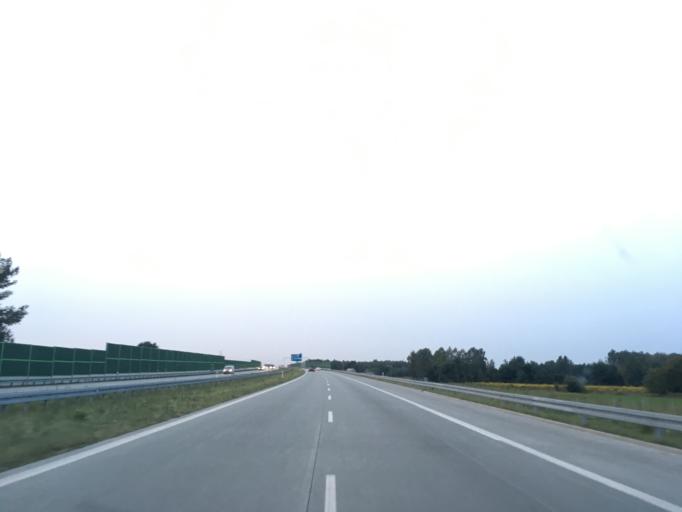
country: PL
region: Lodz Voivodeship
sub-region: Powiat lodzki wschodni
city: Andrespol
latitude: 51.7598
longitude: 19.5953
